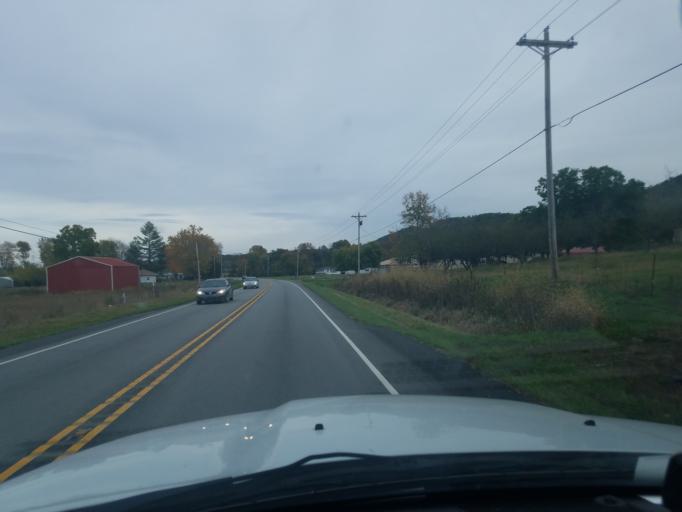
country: US
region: Indiana
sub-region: Clark County
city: Sellersburg
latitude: 38.4444
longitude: -85.8565
